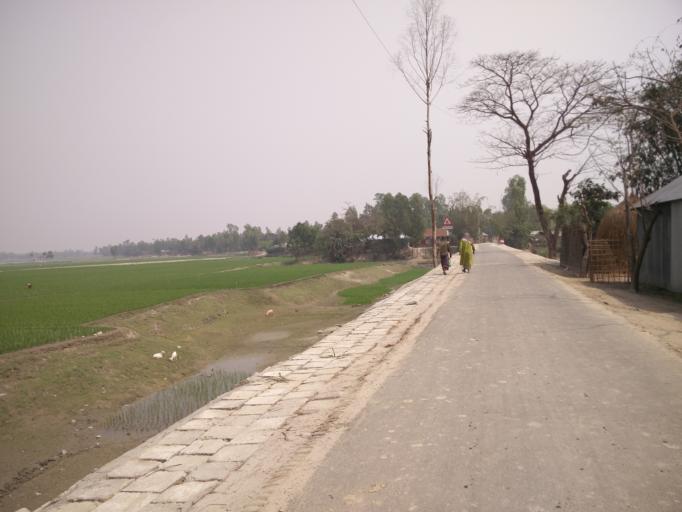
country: BD
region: Rangpur Division
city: Nageswari
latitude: 25.8868
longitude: 89.7351
